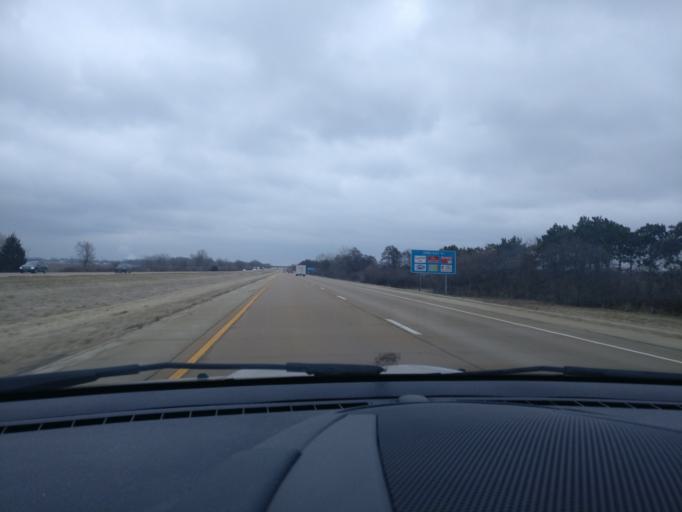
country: US
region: Illinois
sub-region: Whiteside County
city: Rock Falls
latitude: 41.7512
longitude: -89.7252
